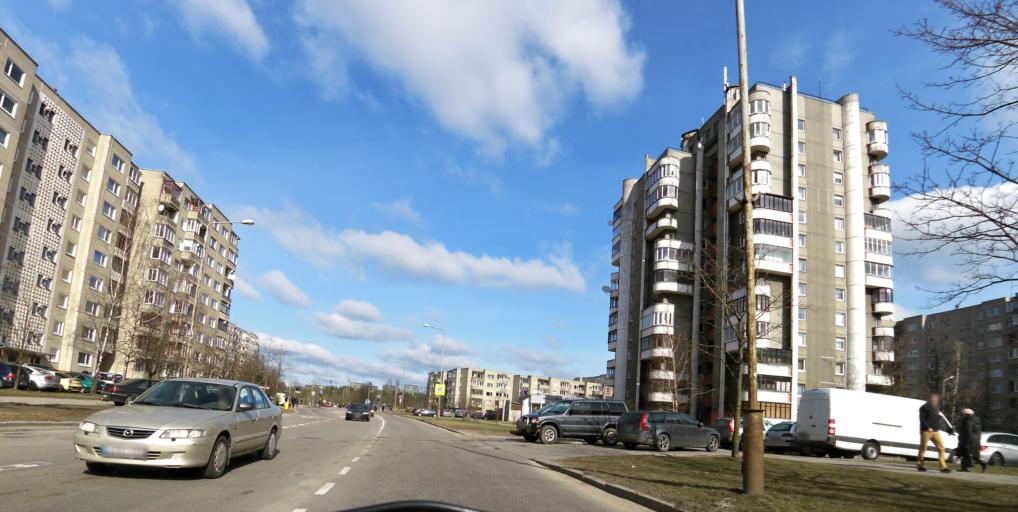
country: LT
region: Vilnius County
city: Seskine
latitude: 54.7169
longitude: 25.2579
